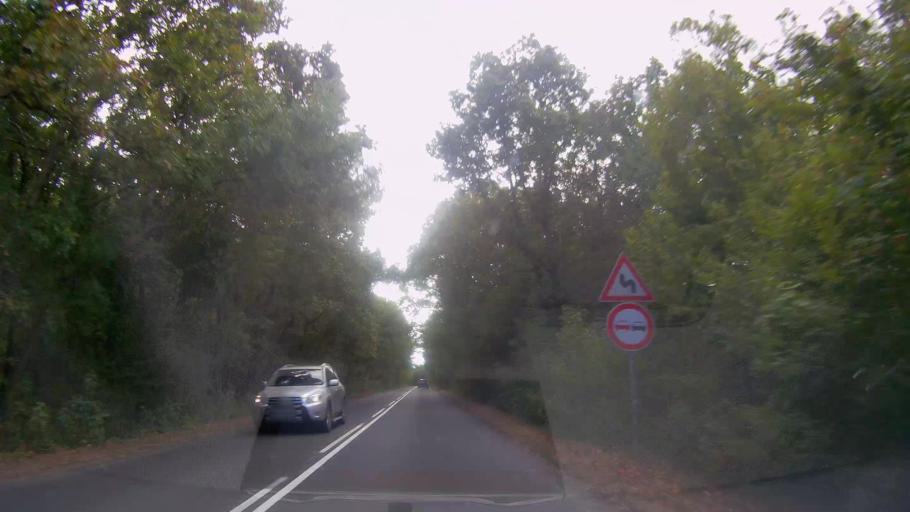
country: BG
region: Burgas
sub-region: Obshtina Primorsko
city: Primorsko
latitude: 42.2967
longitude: 27.7297
